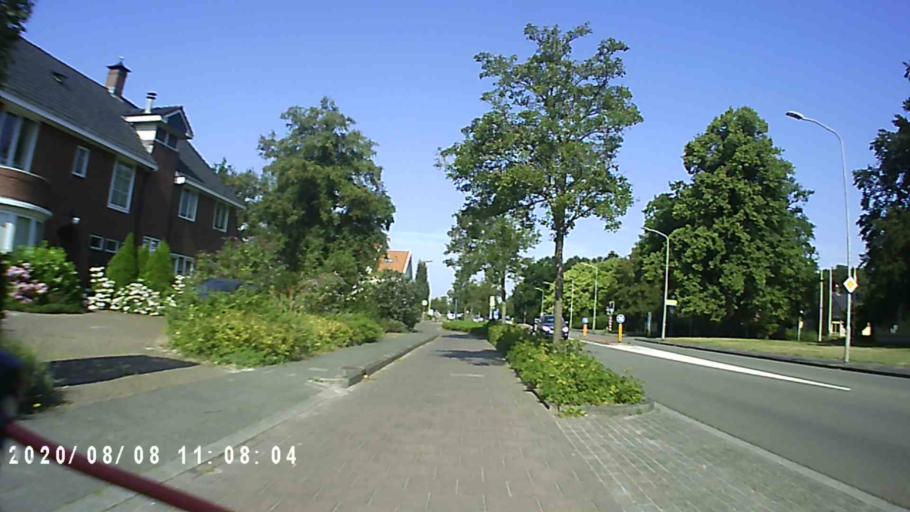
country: NL
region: Groningen
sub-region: Gemeente Leek
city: Leek
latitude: 53.1657
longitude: 6.3860
